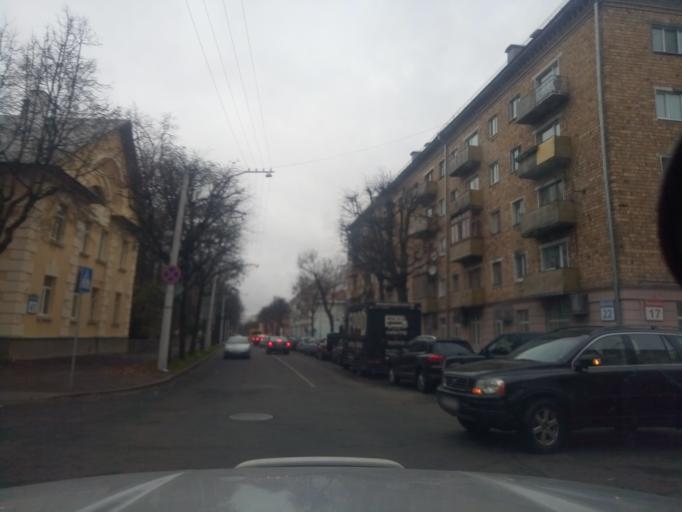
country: BY
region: Minsk
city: Minsk
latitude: 53.9141
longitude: 27.5653
